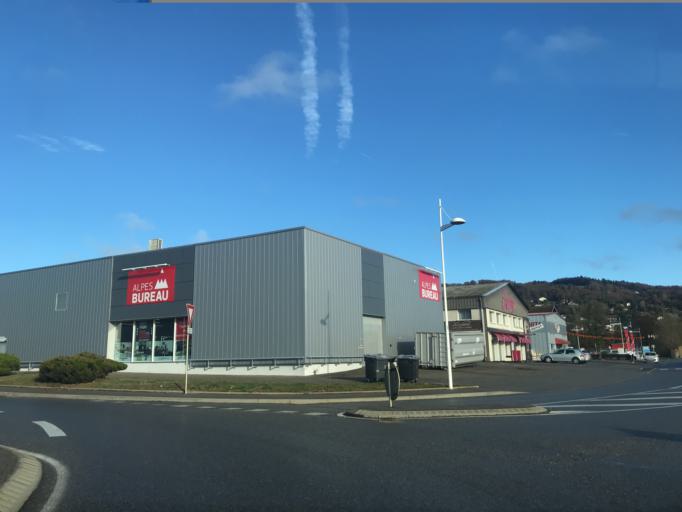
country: FR
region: Rhone-Alpes
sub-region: Departement de la Haute-Savoie
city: Epagny
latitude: 45.9387
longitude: 6.0791
